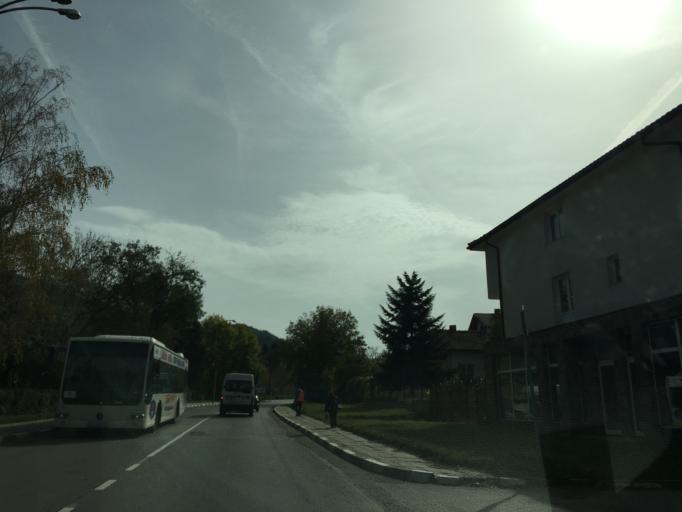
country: BG
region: Sofia-Capital
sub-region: Stolichna Obshtina
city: Sofia
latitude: 42.5850
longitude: 23.4221
